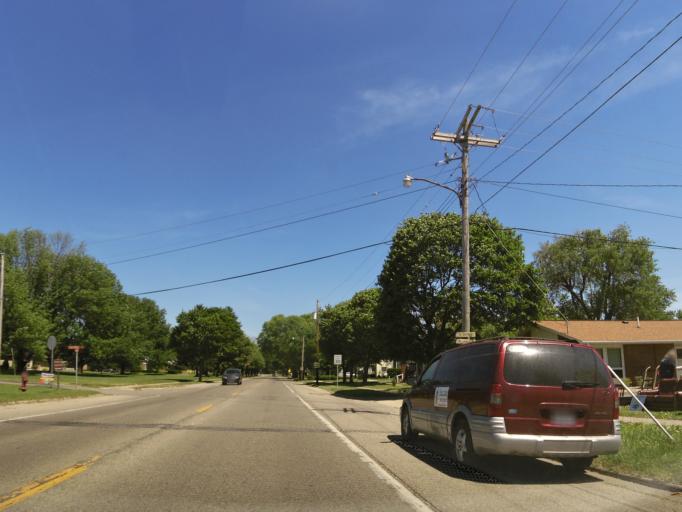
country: US
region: Illinois
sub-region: Vermilion County
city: Rossville
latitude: 40.3727
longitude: -87.6671
